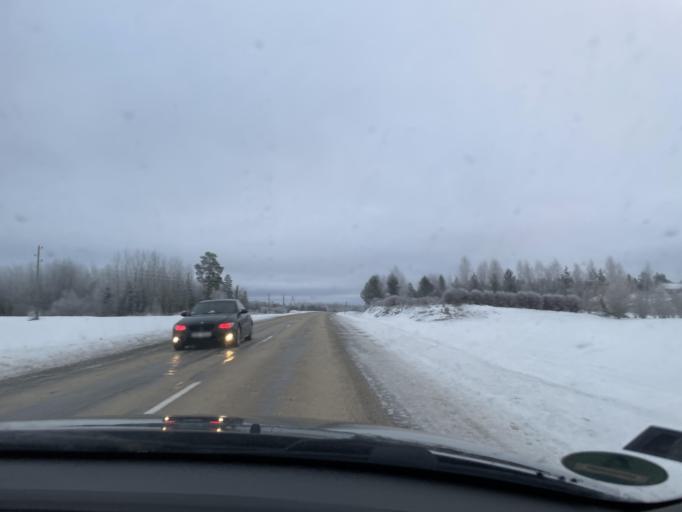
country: LV
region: Rezekne
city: Rezekne
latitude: 56.4963
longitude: 27.4170
